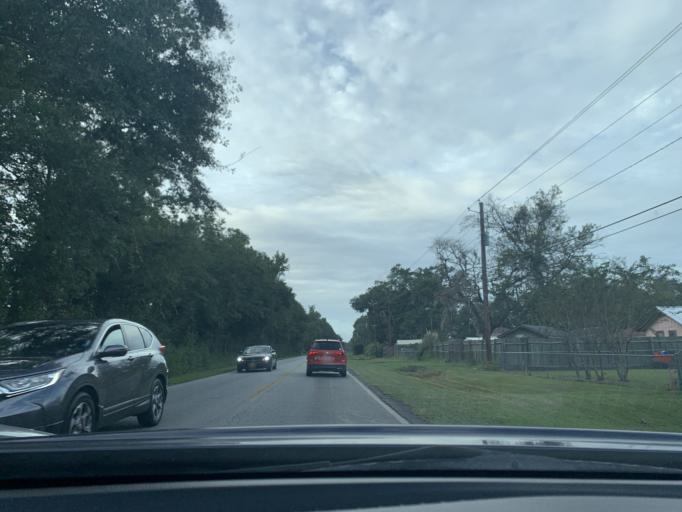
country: US
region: Georgia
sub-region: Chatham County
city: Georgetown
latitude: 32.0238
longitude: -81.2435
